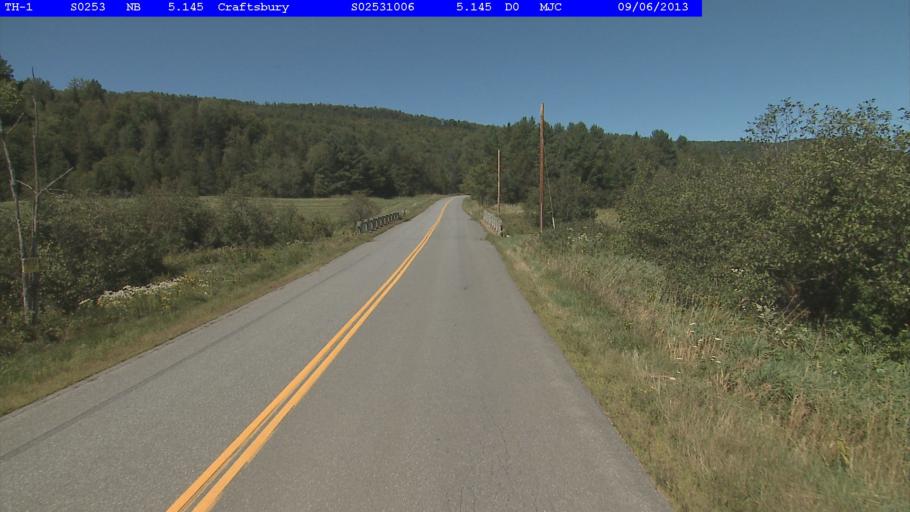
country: US
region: Vermont
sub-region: Caledonia County
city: Hardwick
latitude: 44.6769
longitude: -72.4001
